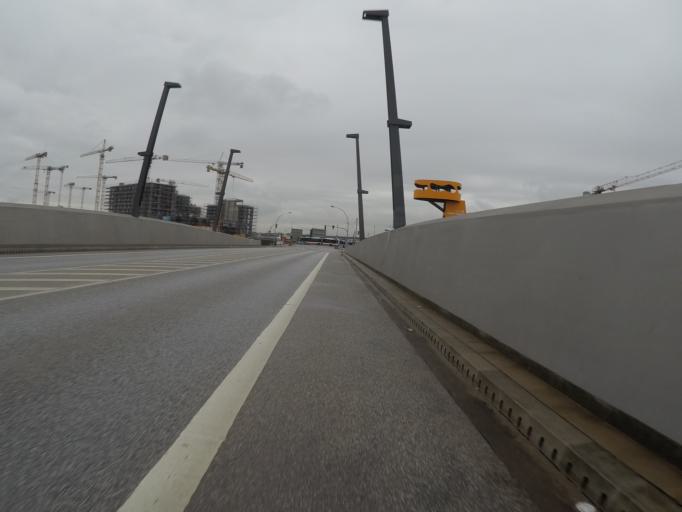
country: DE
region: Hamburg
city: Altstadt
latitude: 53.5391
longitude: 10.0080
